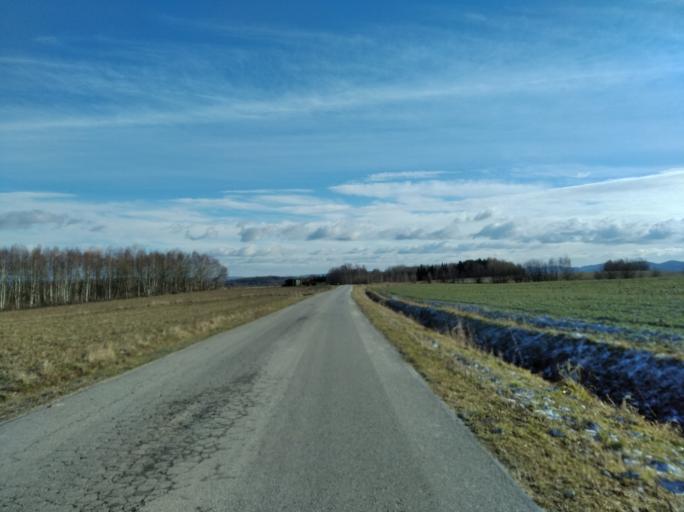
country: PL
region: Subcarpathian Voivodeship
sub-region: Powiat strzyzowski
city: Wisniowa
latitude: 49.9071
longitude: 21.6465
